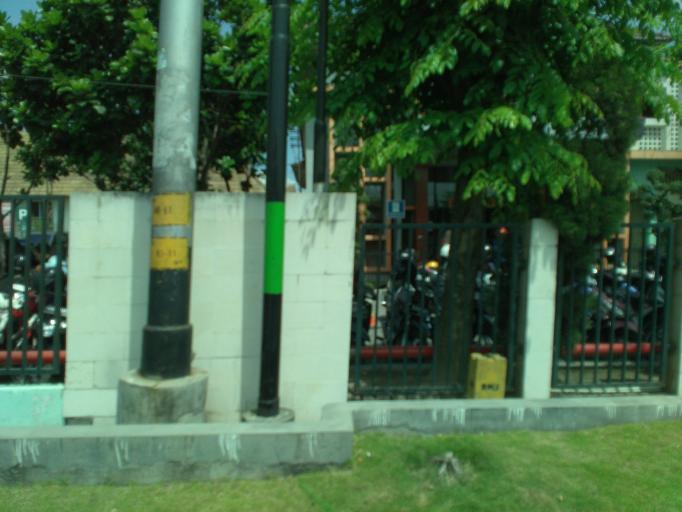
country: ID
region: Central Java
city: Klaten
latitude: -7.7149
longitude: 110.5889
